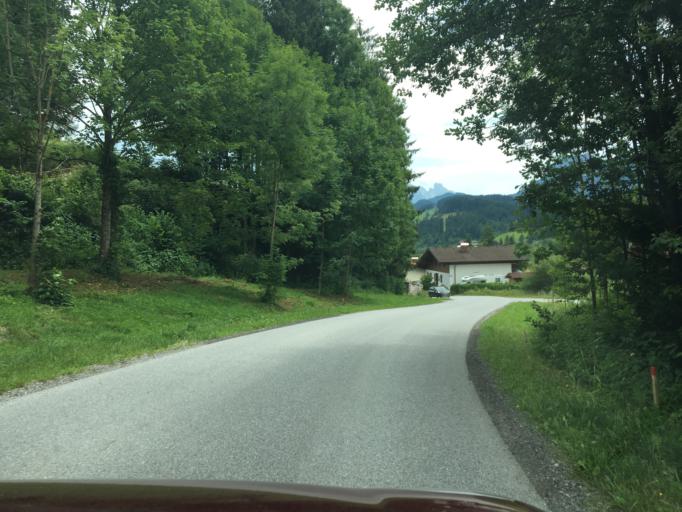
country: AT
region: Salzburg
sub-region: Politischer Bezirk Hallein
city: Abtenau
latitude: 47.5982
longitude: 13.3034
